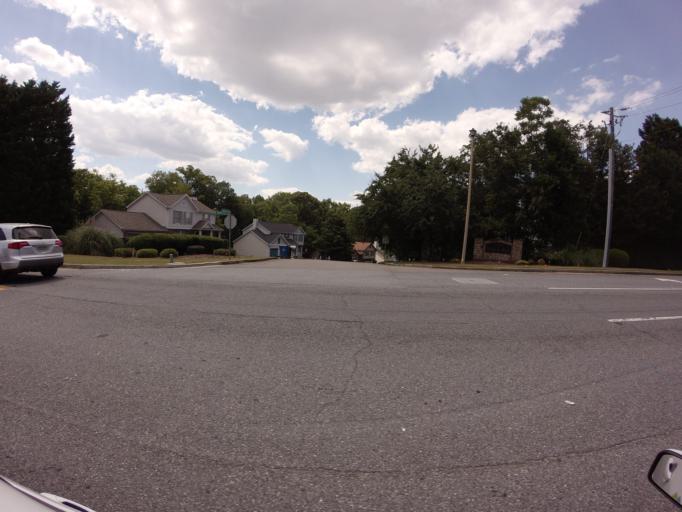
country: US
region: Georgia
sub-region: Fulton County
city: Johns Creek
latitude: 34.0343
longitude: -84.2409
